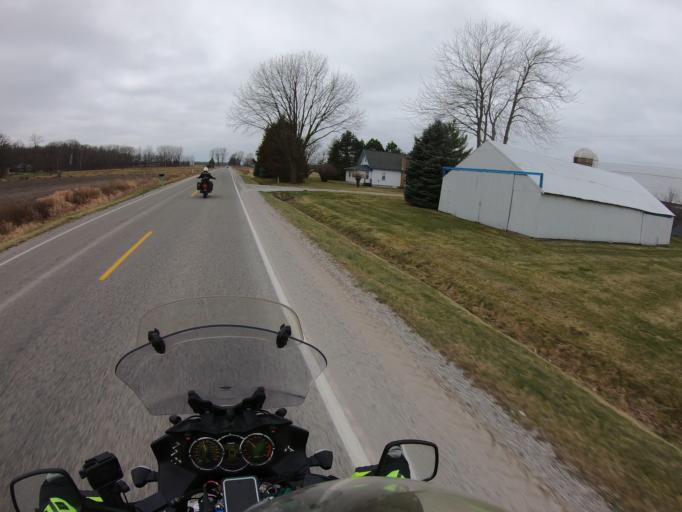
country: US
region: Michigan
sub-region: Saginaw County
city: Saint Charles
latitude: 43.2560
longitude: -84.0737
